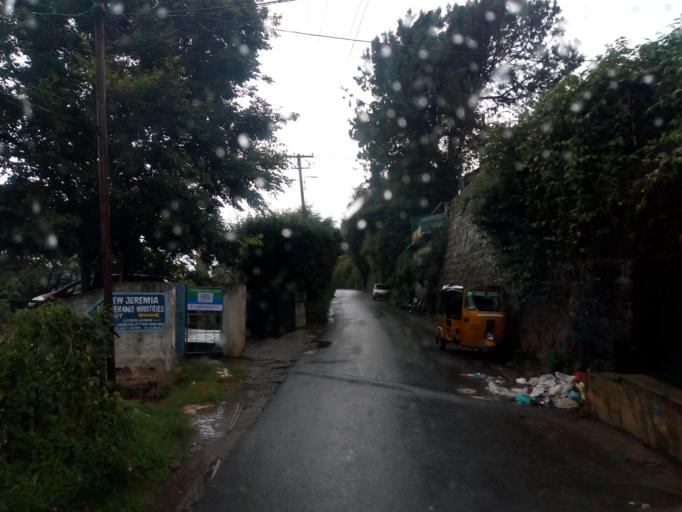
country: IN
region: Tamil Nadu
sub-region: Nilgiri
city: Wellington
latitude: 11.3482
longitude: 76.8017
